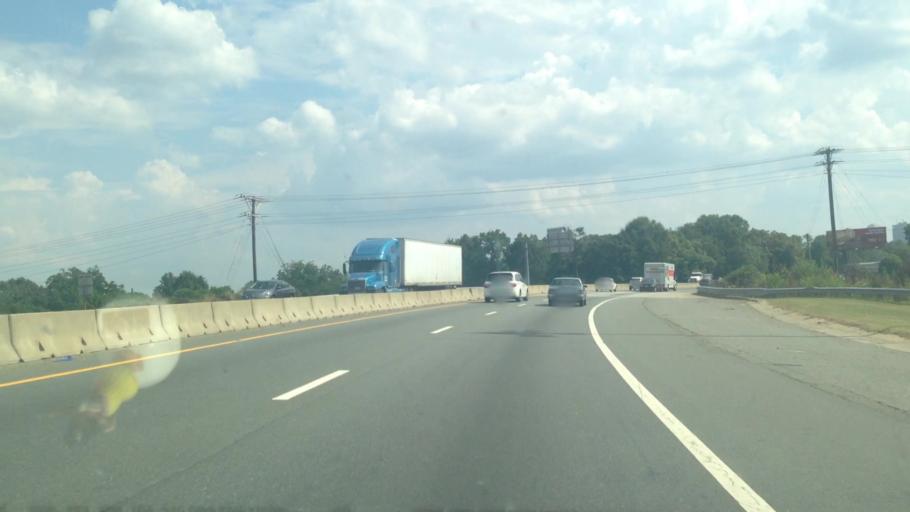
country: US
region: North Carolina
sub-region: Forsyth County
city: Winston-Salem
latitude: 36.1229
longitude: -80.2322
